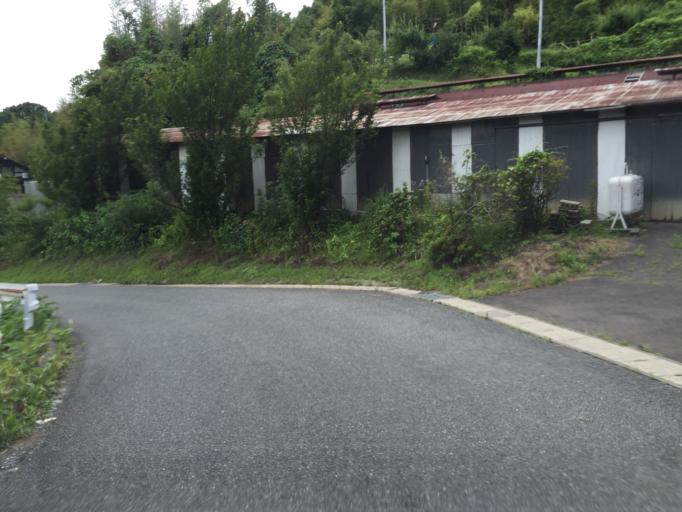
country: JP
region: Fukushima
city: Fukushima-shi
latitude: 37.6784
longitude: 140.5082
